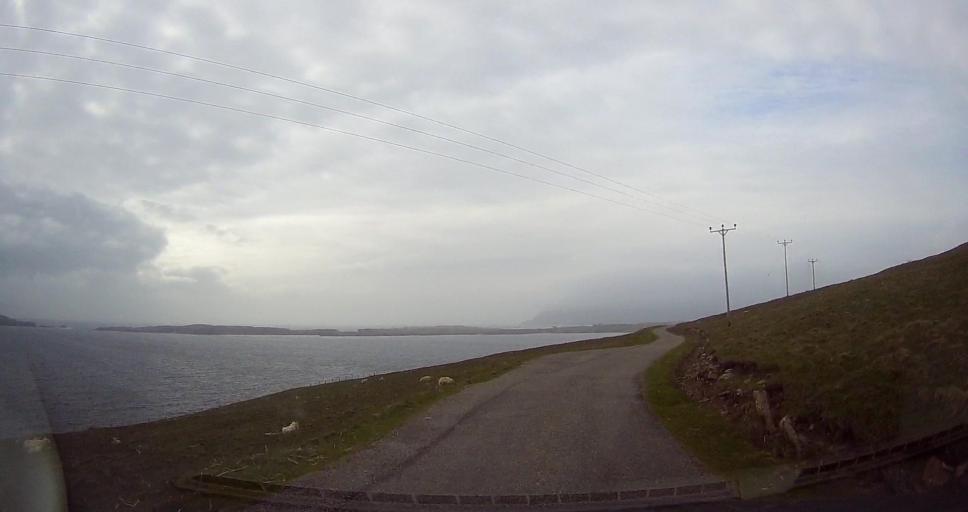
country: GB
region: Scotland
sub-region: Shetland Islands
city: Sandwick
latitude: 59.8588
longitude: -1.2755
